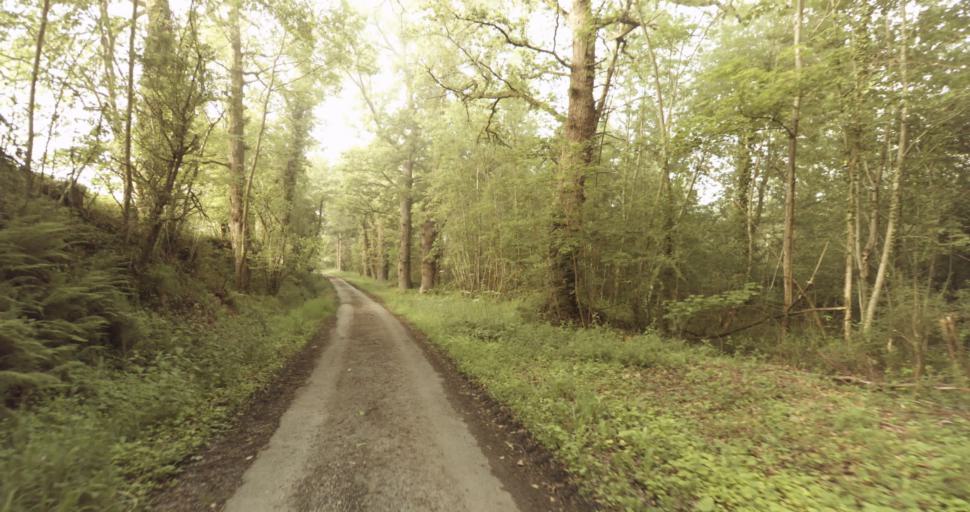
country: FR
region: Limousin
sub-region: Departement de la Haute-Vienne
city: Le Vigen
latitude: 45.7609
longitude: 1.2900
